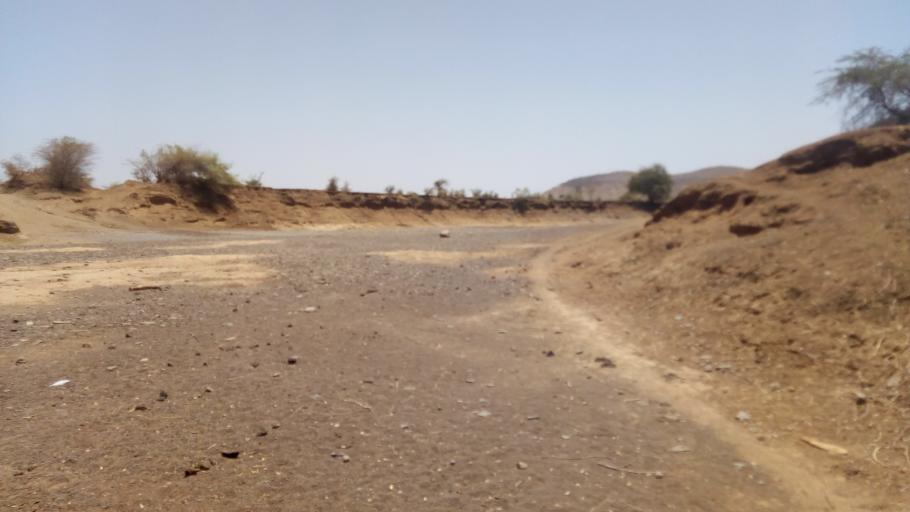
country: ML
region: Kayes
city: Yelimane
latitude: 14.6514
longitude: -10.6941
